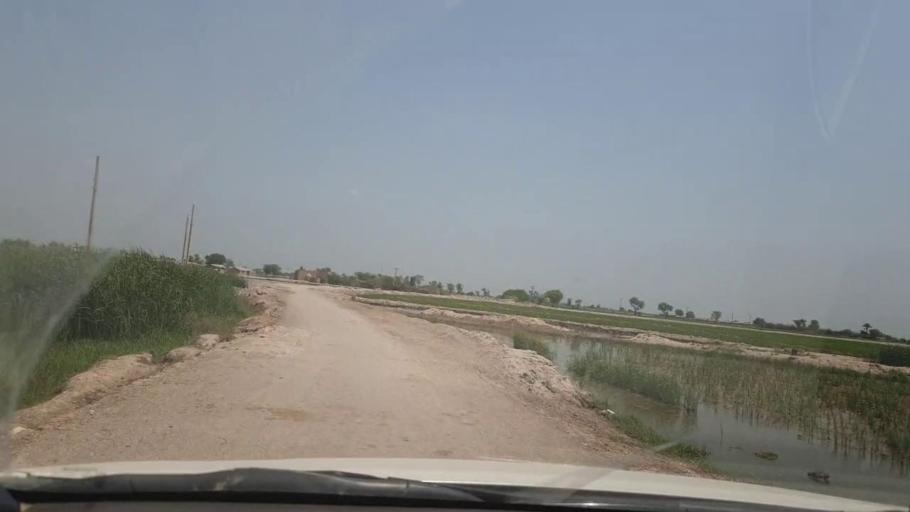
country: PK
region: Sindh
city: Lakhi
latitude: 27.8774
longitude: 68.7335
